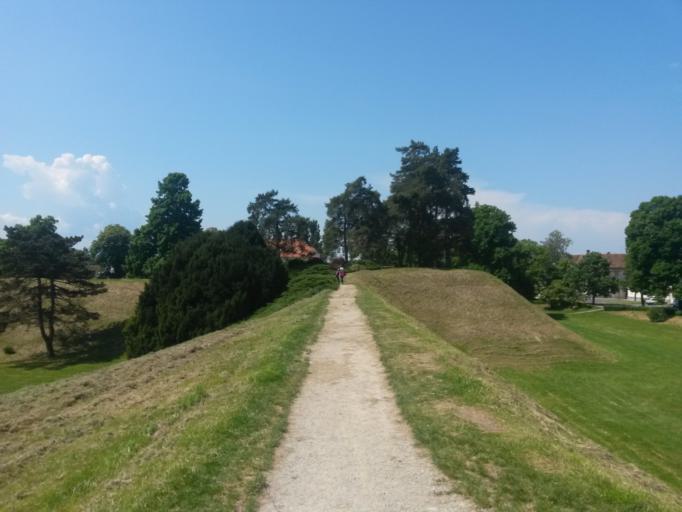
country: HR
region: Varazdinska
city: Varazdin
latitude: 46.3106
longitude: 16.3339
